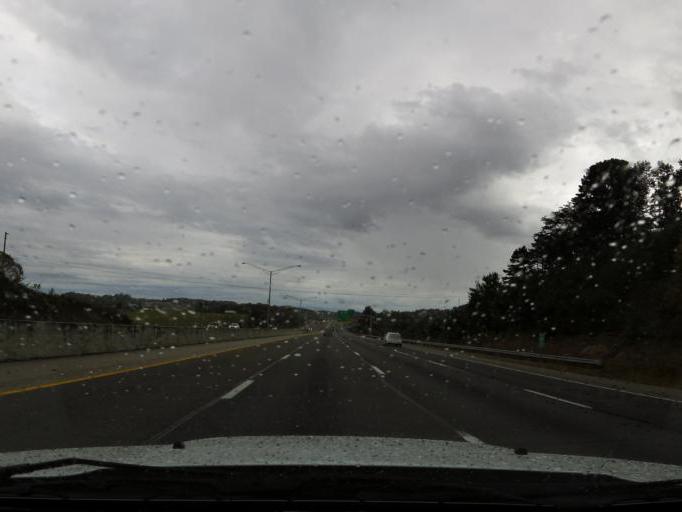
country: US
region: Kentucky
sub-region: Laurel County
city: London
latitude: 37.1356
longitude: -84.1091
